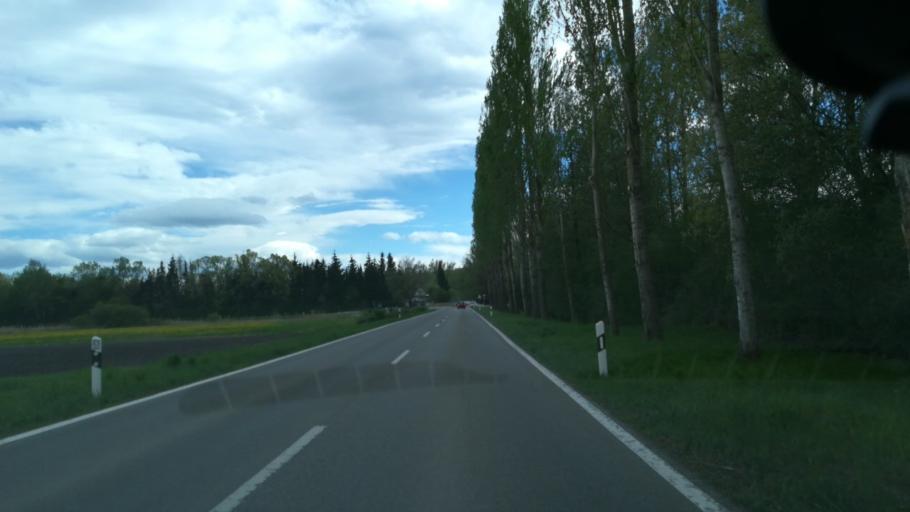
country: DE
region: Baden-Wuerttemberg
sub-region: Freiburg Region
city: Moos
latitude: 47.7444
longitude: 8.9260
